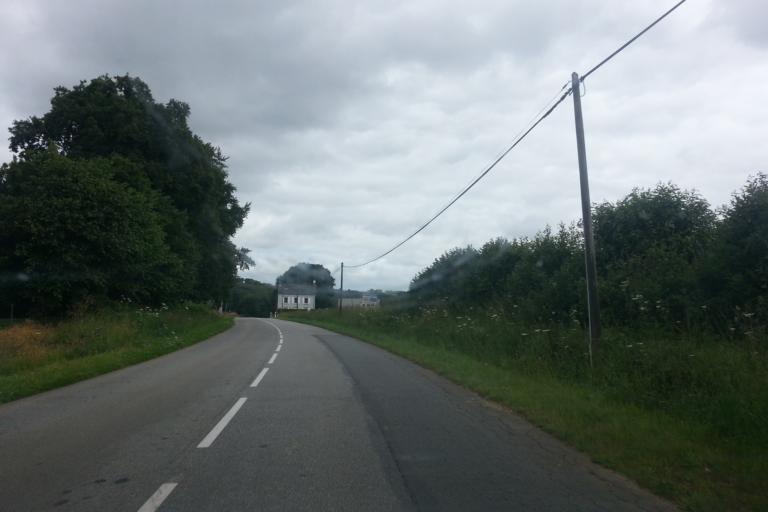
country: FR
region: Brittany
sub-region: Departement du Finistere
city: Edern
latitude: 48.0979
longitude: -3.9840
